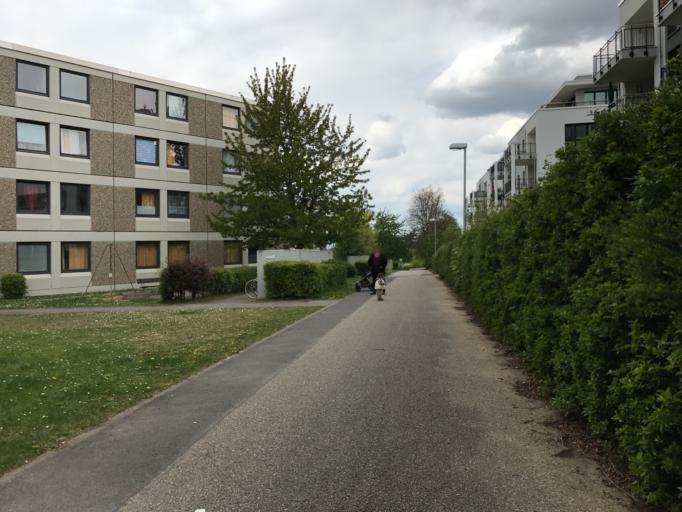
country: DE
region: Rheinland-Pfalz
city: Mainz
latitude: 49.9777
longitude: 8.2649
